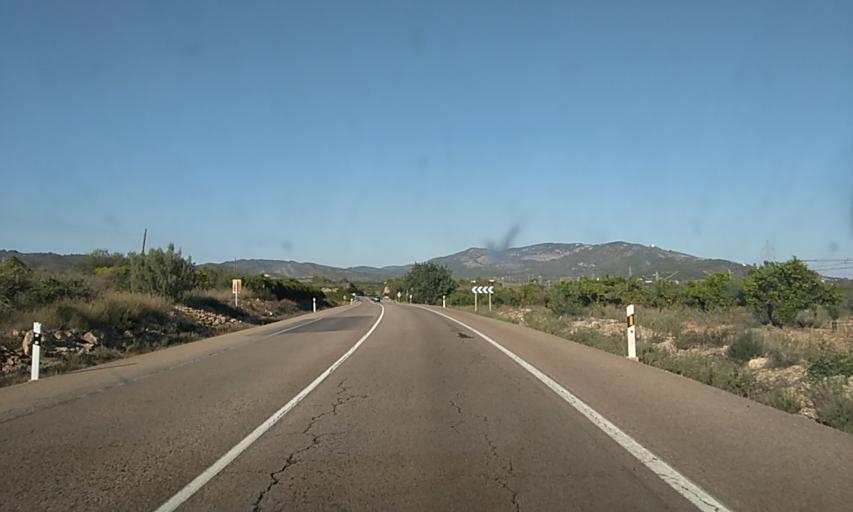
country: ES
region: Valencia
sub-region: Provincia de Castello
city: Torreblanca
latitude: 40.2349
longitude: 0.2222
